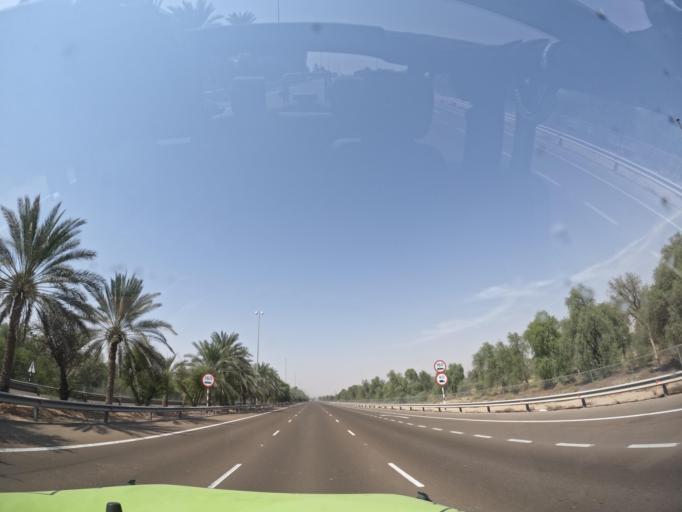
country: AE
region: Abu Dhabi
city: Al Ain
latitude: 24.1742
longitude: 55.2959
